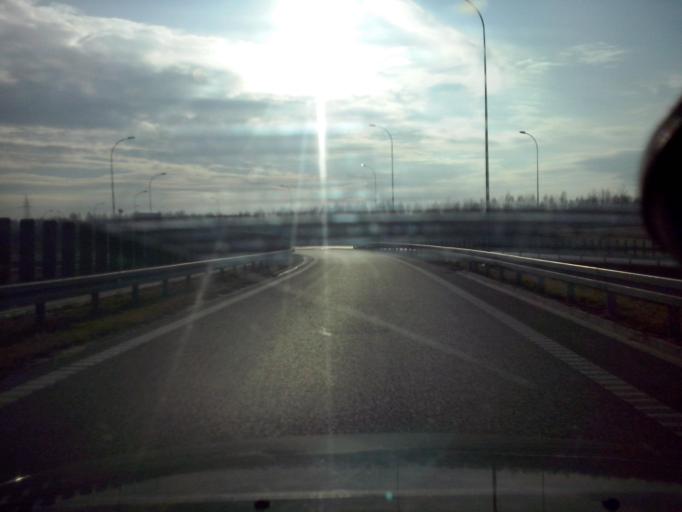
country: PL
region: Subcarpathian Voivodeship
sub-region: Powiat rzeszowski
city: Rudna Wielka
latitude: 50.1046
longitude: 21.9205
